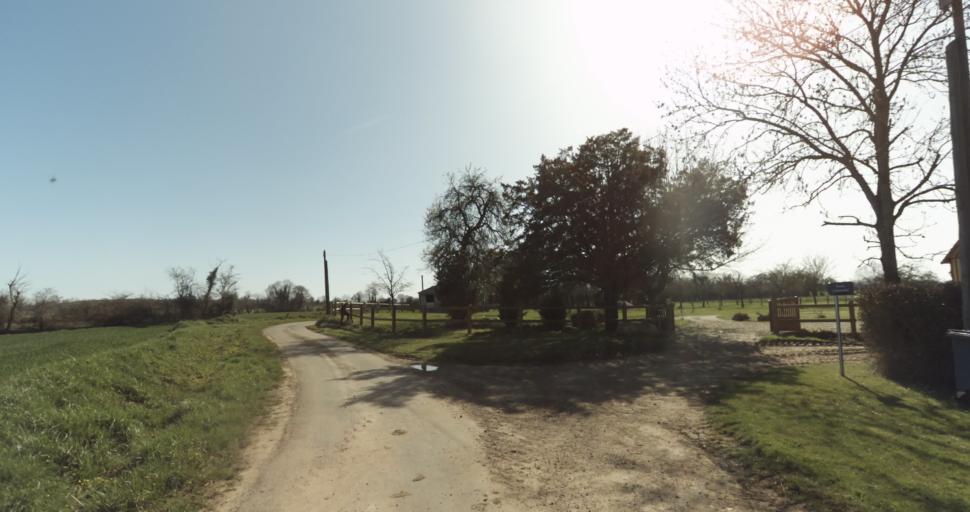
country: FR
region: Lower Normandy
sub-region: Departement de l'Orne
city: Trun
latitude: 48.9302
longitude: 0.0020
